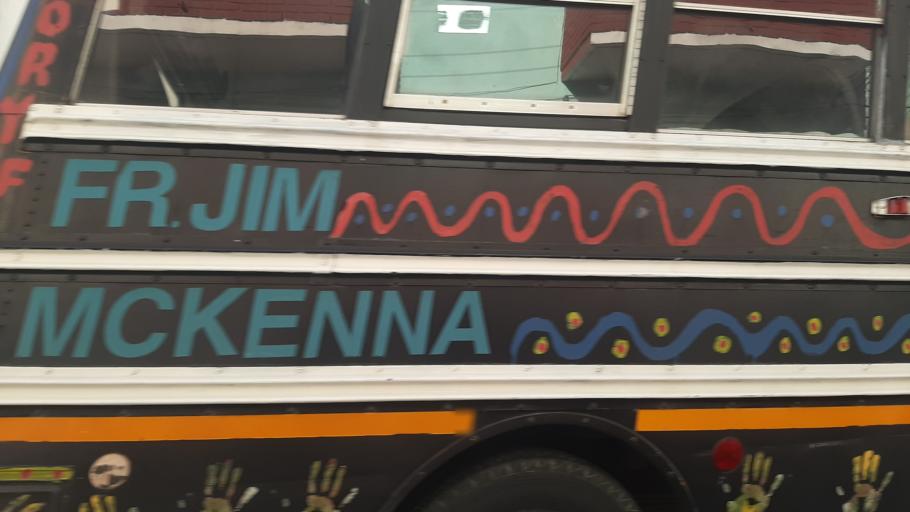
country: CU
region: Villa Clara
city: Santa Clara
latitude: 22.4091
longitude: -79.9624
